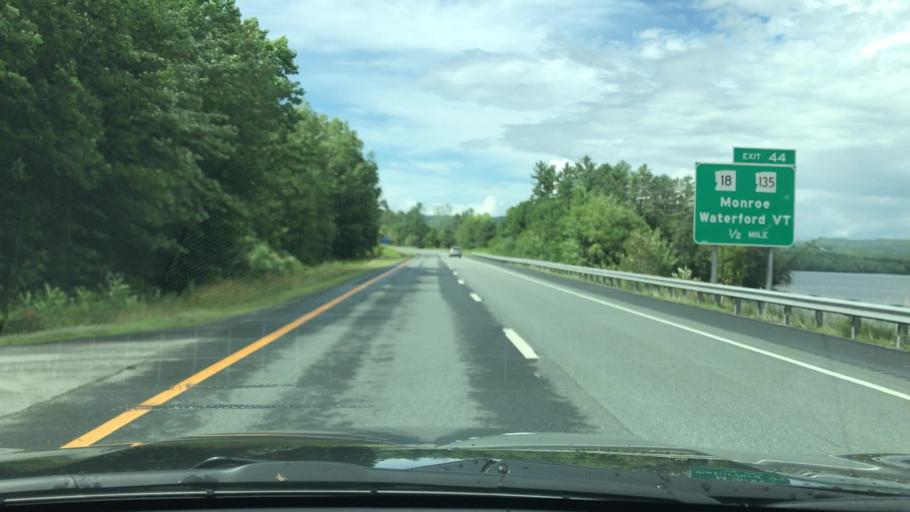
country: US
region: New Hampshire
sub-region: Grafton County
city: Littleton
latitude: 44.3231
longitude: -71.8677
